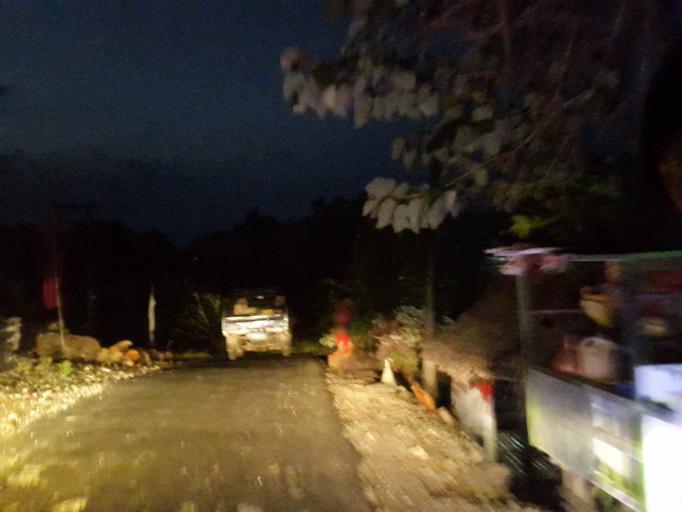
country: ID
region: Bali
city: Kutampi
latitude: -8.6816
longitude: 115.5427
